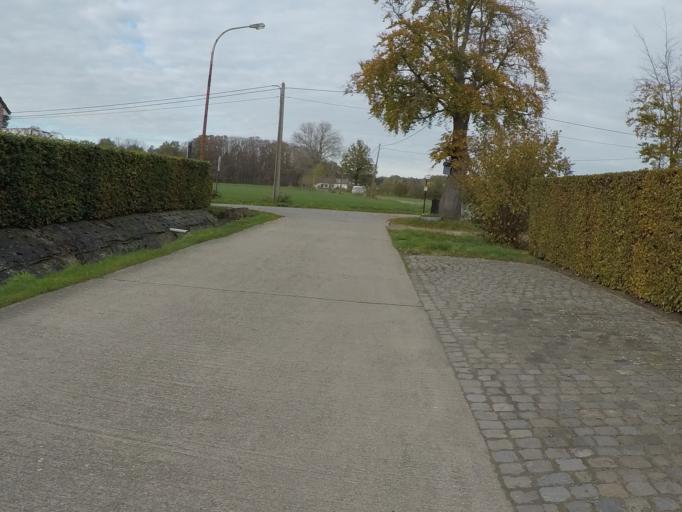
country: BE
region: Flanders
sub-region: Provincie Antwerpen
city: Nijlen
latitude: 51.1421
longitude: 4.6909
